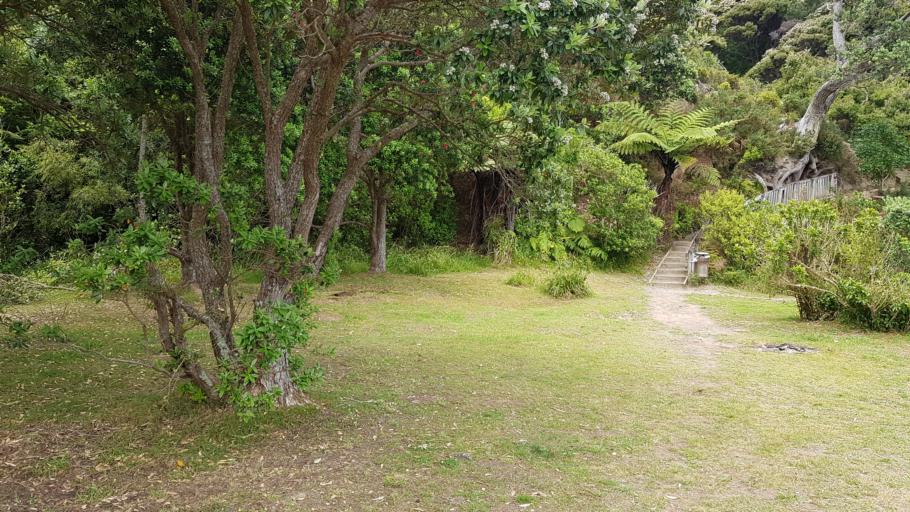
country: NZ
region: Auckland
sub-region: Auckland
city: North Shore
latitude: -36.8236
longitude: 174.7078
